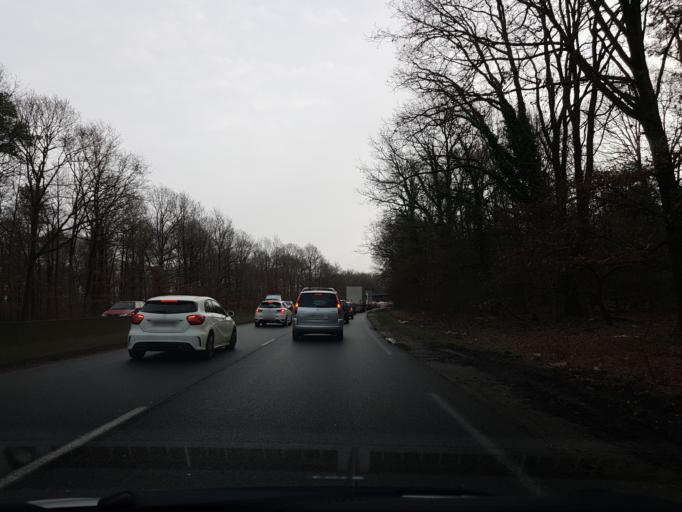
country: FR
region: Ile-de-France
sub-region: Departement de l'Essonne
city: Brunoy
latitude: 48.6891
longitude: 2.4786
